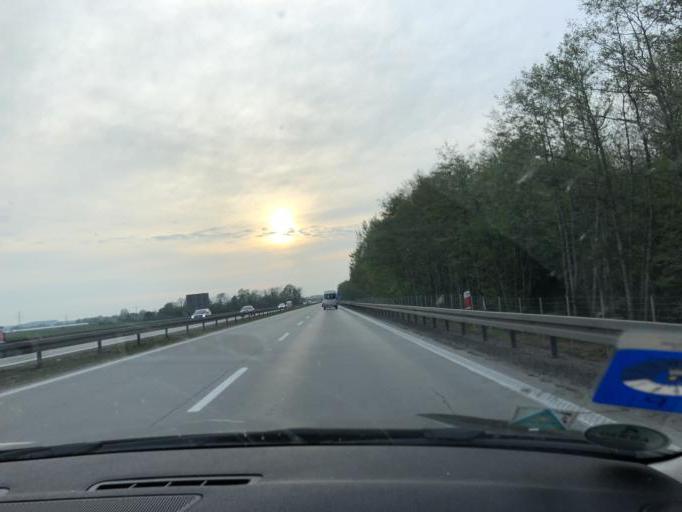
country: PL
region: Lower Silesian Voivodeship
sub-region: Legnica
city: Legnica
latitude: 51.1651
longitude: 16.1144
